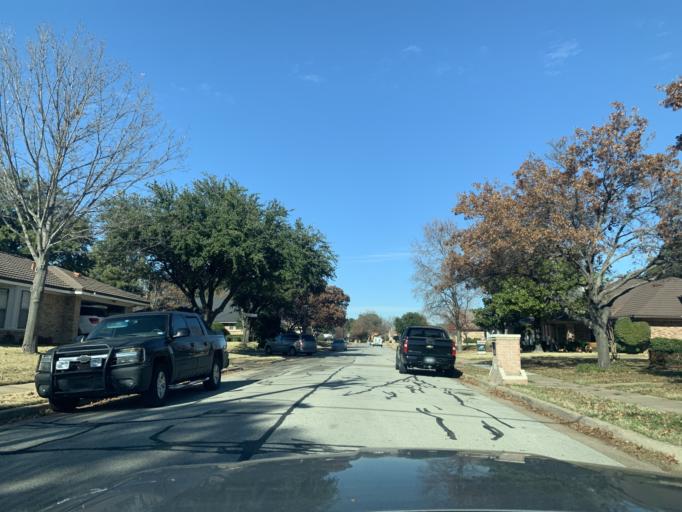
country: US
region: Texas
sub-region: Tarrant County
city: Bedford
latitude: 32.8429
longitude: -97.1535
